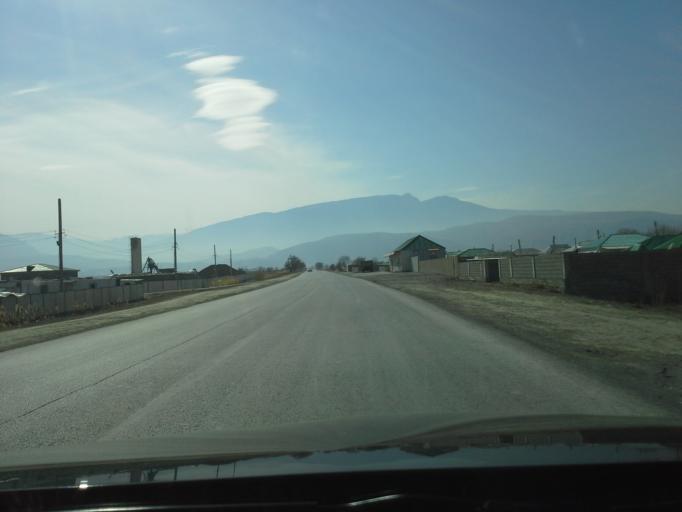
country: TM
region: Ahal
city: Abadan
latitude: 38.1035
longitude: 58.0276
